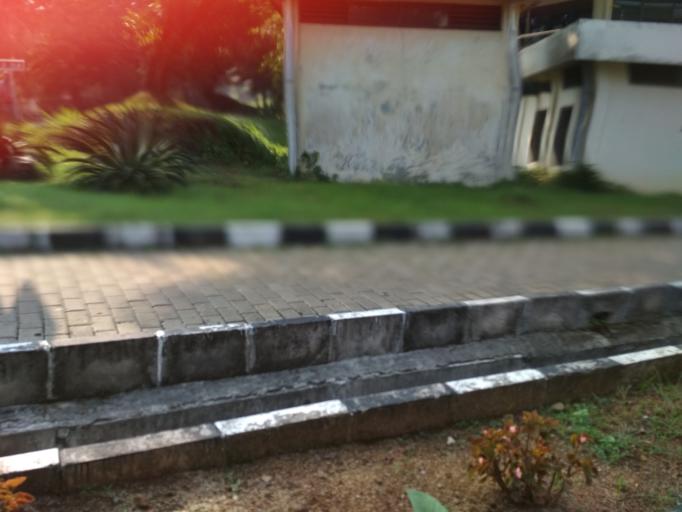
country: ID
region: West Java
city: Ciampea
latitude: -6.5582
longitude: 106.7269
